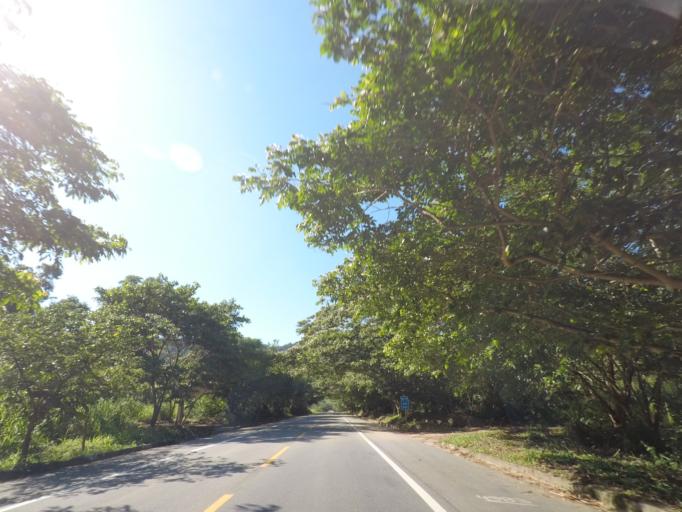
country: BR
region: Rio de Janeiro
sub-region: Parati
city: Paraty
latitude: -23.2538
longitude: -44.6995
